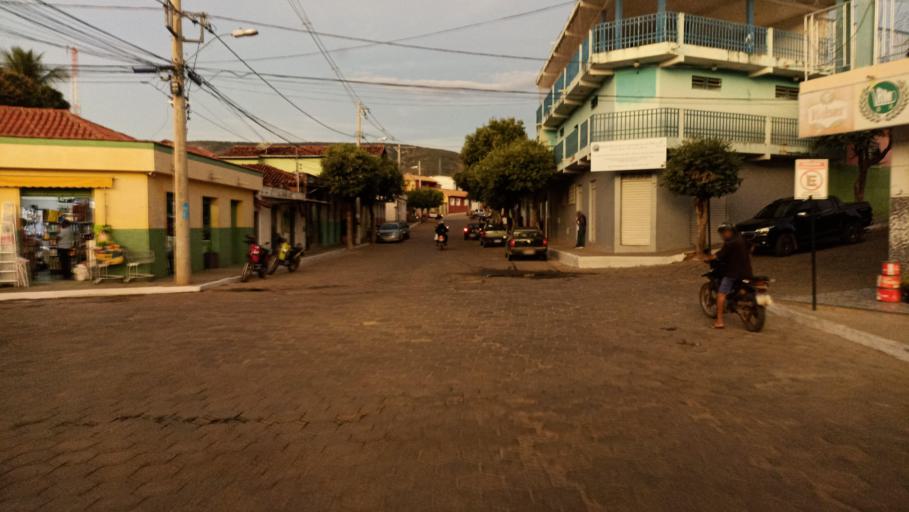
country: BR
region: Minas Gerais
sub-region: Aracuai
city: Aracuai
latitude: -16.6170
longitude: -42.1823
